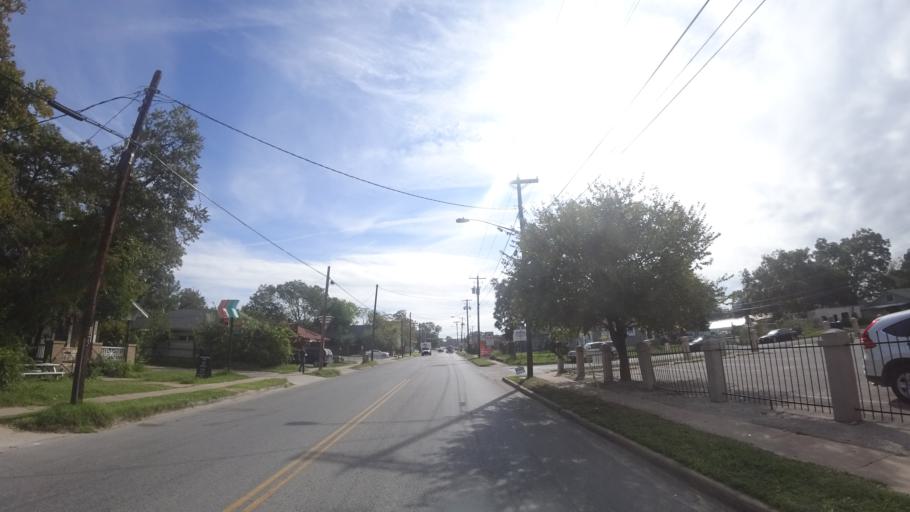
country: US
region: Texas
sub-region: Travis County
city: Austin
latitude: 30.2536
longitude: -97.7144
